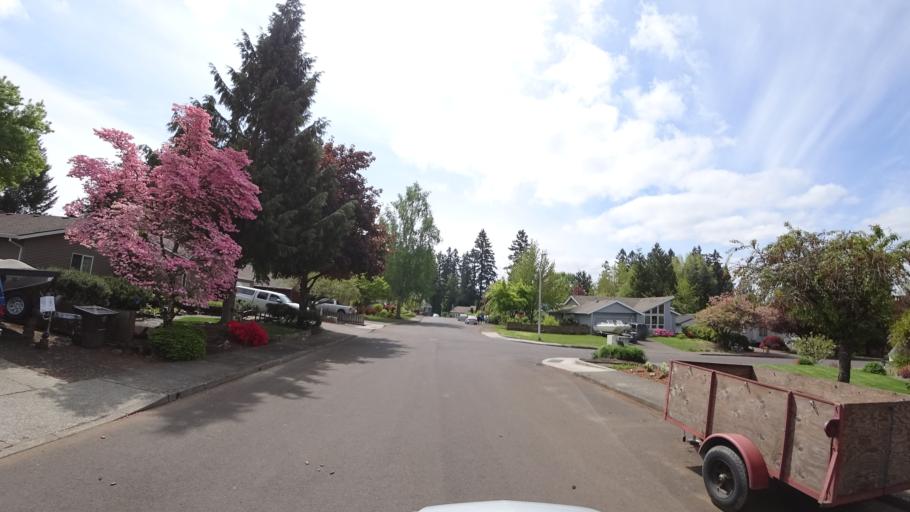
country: US
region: Oregon
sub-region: Washington County
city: Hillsboro
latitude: 45.5388
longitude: -122.9900
